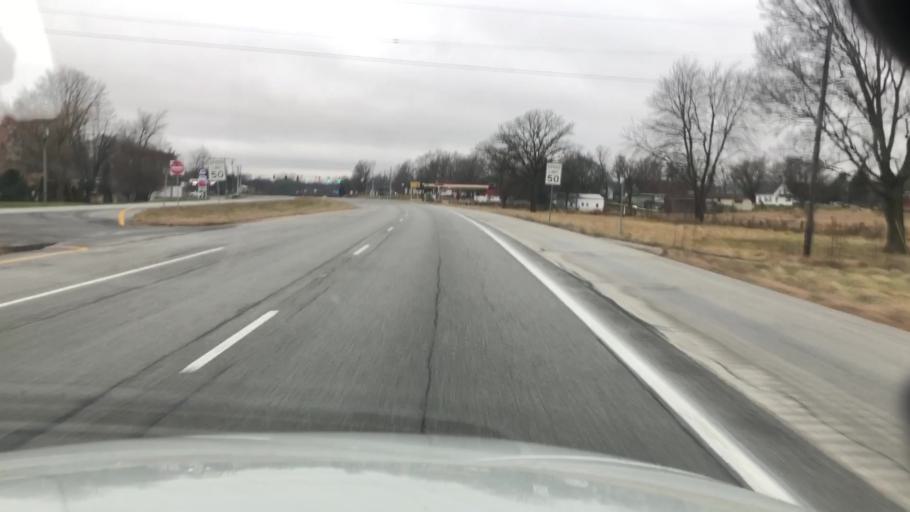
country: US
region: Indiana
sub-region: Kosciusko County
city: Pierceton
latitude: 41.1810
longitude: -85.6220
